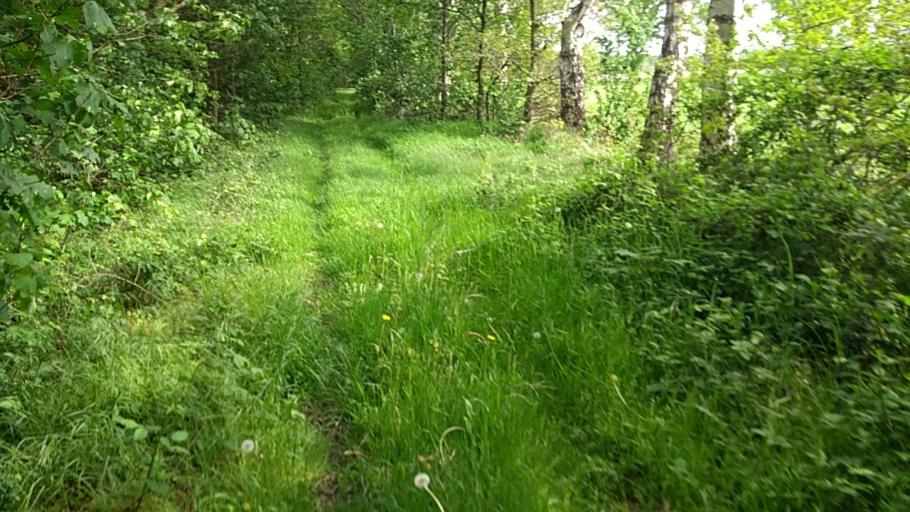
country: NL
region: Limburg
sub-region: Gemeente Leudal
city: Kelpen-Oler
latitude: 51.2876
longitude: 5.8221
